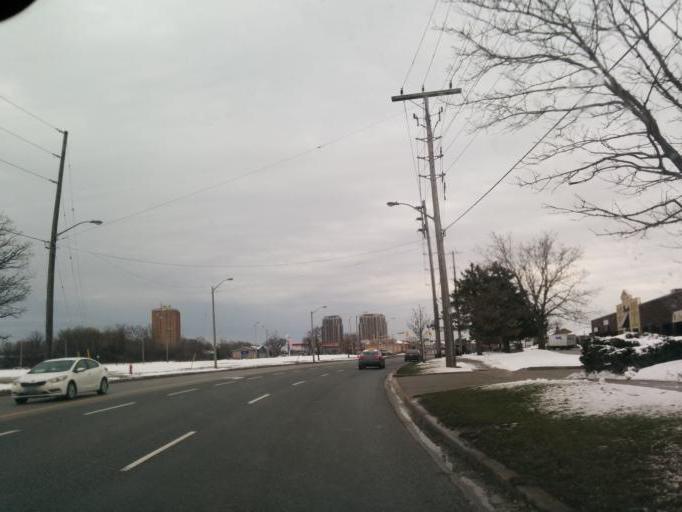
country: CA
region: Ontario
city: Etobicoke
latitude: 43.7366
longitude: -79.6178
